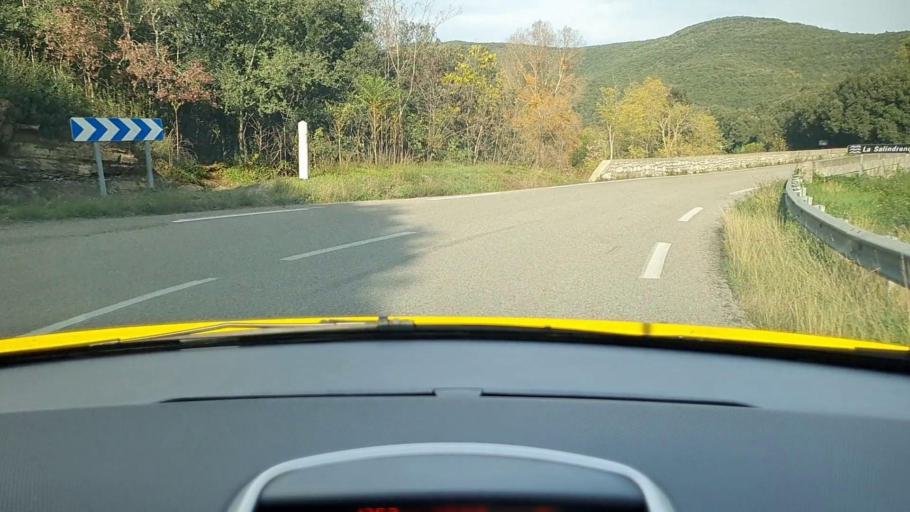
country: FR
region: Languedoc-Roussillon
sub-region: Departement du Gard
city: Anduze
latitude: 44.0704
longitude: 3.9345
